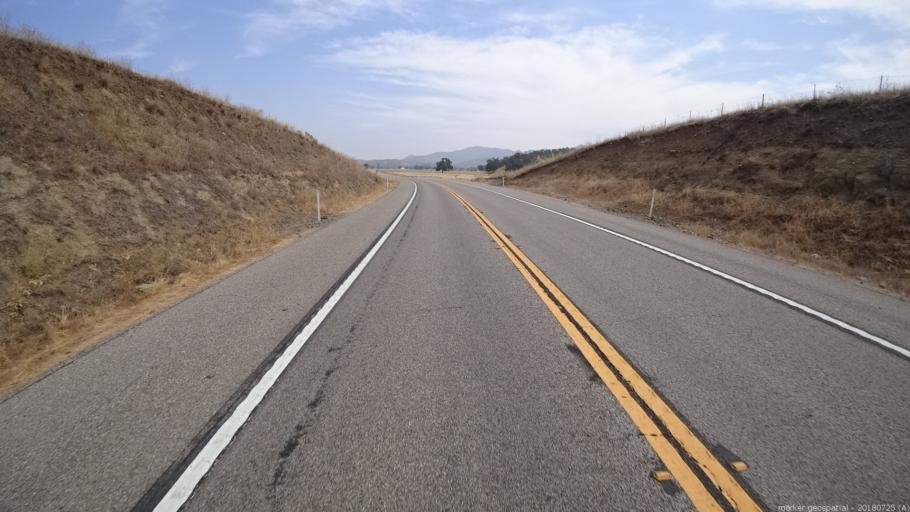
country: US
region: California
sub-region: Fresno County
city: Coalinga
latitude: 36.1862
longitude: -120.7043
